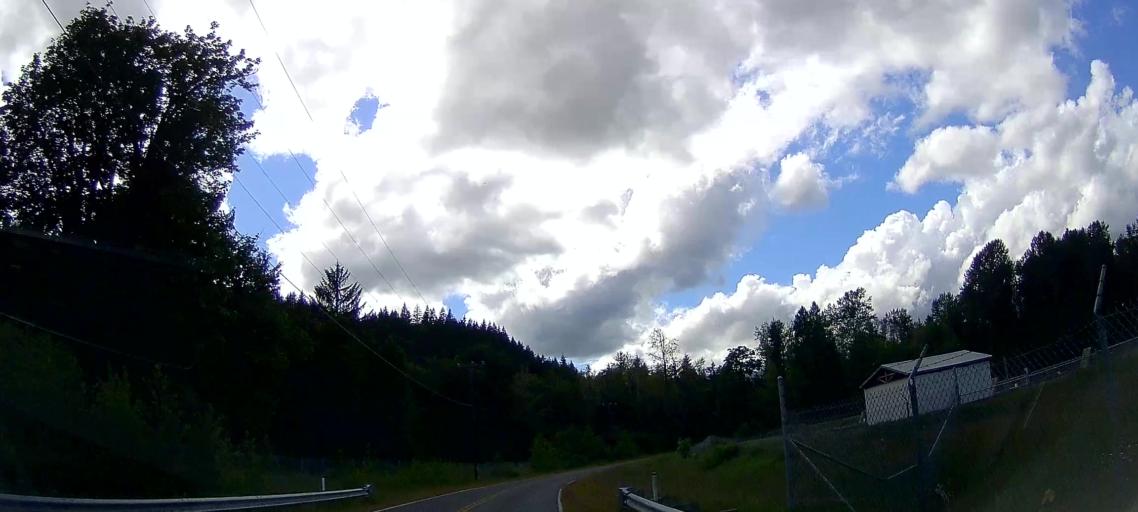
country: US
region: Washington
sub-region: Skagit County
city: Sedro-Woolley
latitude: 48.6709
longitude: -122.1438
